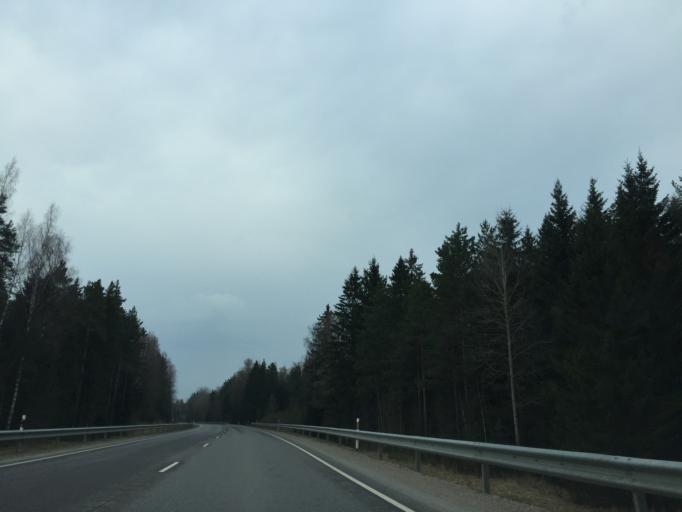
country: EE
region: Tartu
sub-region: UElenurme vald
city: Ulenurme
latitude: 58.1009
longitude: 26.7404
